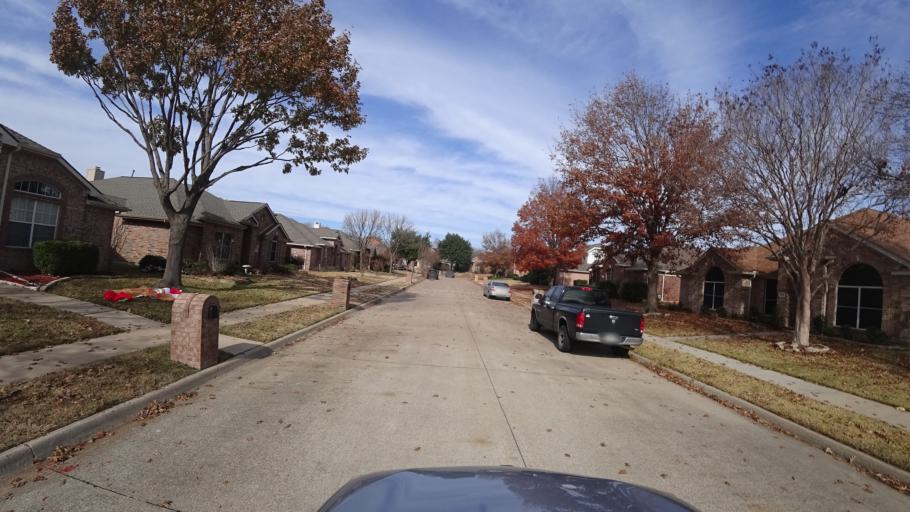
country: US
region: Texas
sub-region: Denton County
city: Highland Village
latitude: 33.0642
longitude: -97.0371
